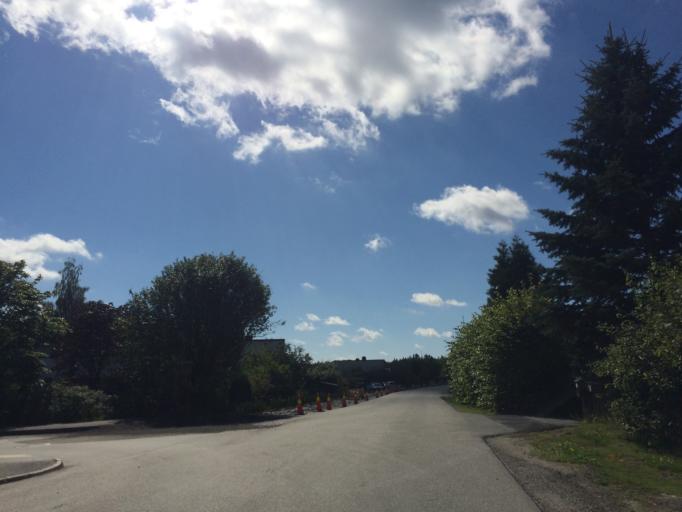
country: NO
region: Akershus
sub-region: Ski
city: Ski
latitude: 59.7161
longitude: 10.8145
